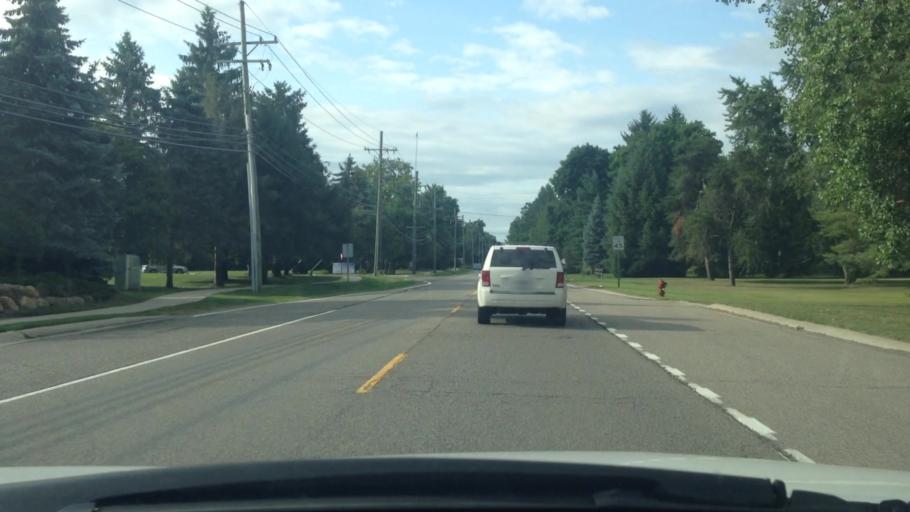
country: US
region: Michigan
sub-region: Oakland County
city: Waterford
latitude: 42.7130
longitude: -83.3490
